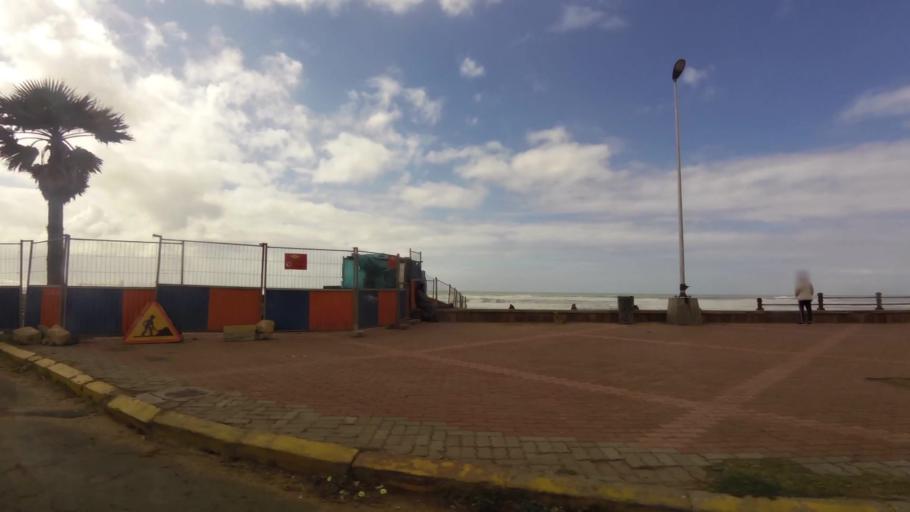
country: MA
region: Grand Casablanca
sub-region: Casablanca
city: Casablanca
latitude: 33.5851
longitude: -7.6890
